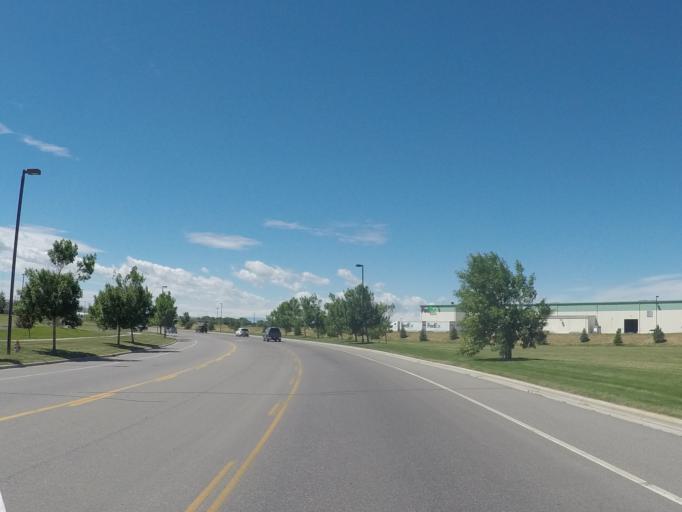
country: US
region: Montana
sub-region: Yellowstone County
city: Billings
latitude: 45.7435
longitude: -108.6058
